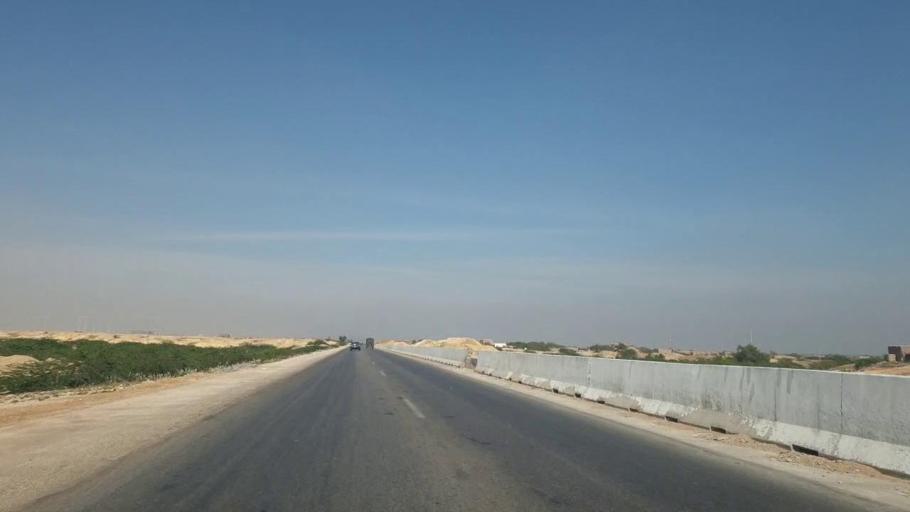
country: PK
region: Sindh
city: Matiari
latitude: 25.6679
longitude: 68.2956
